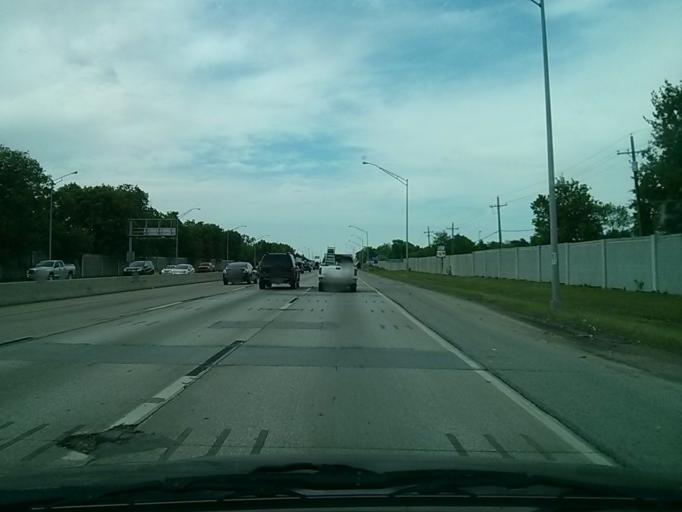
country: US
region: Oklahoma
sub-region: Tulsa County
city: Broken Arrow
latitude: 36.1227
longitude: -95.8595
